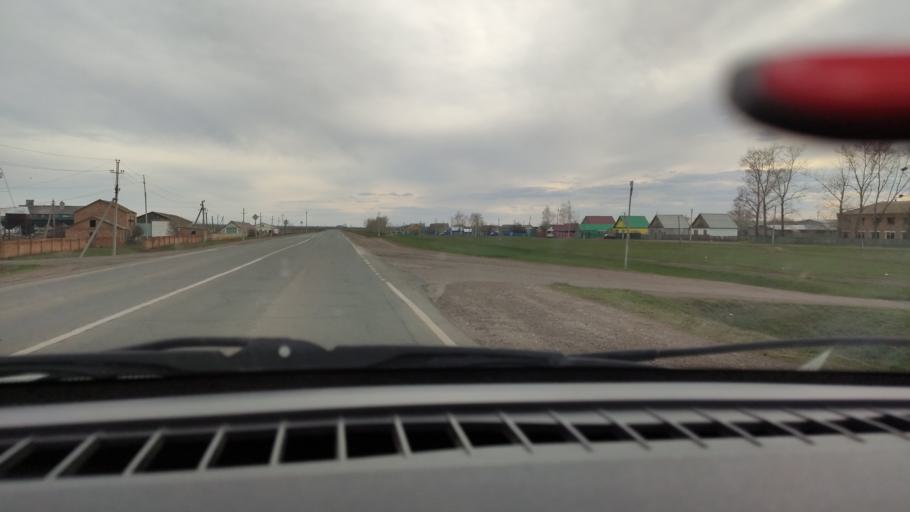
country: RU
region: Bashkortostan
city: Mayachnyy
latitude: 52.4225
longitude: 55.7783
